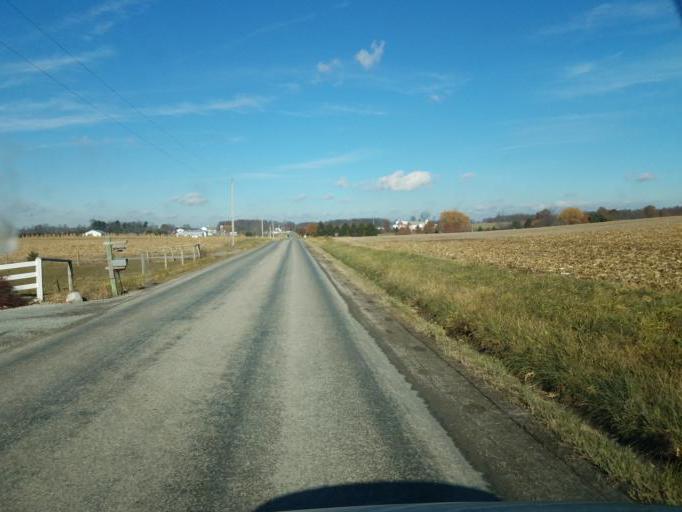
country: US
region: Ohio
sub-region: Wayne County
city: Apple Creek
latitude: 40.7586
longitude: -81.7753
